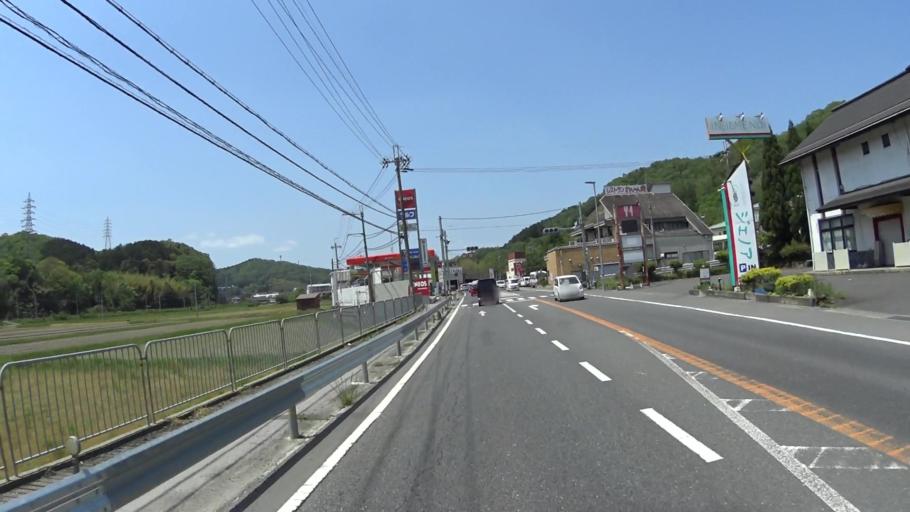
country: JP
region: Kyoto
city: Kameoka
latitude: 35.0932
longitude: 135.4945
